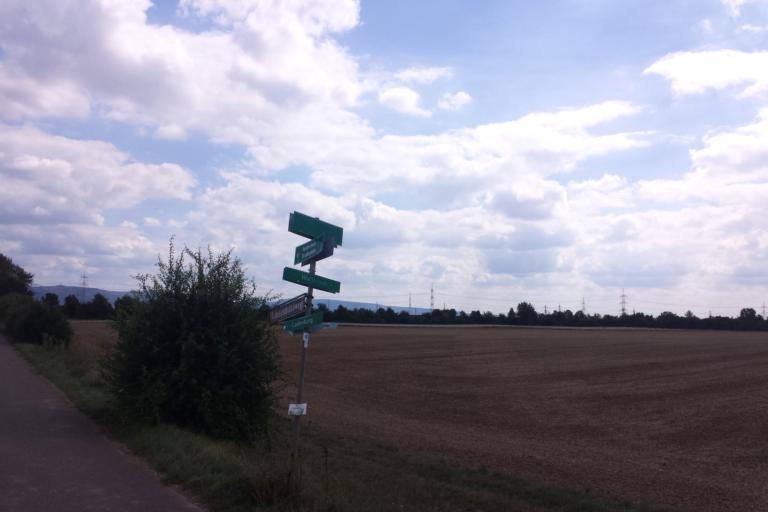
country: DE
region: Baden-Wuerttemberg
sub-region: Karlsruhe Region
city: Ilvesheim
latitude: 49.5052
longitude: 8.5570
